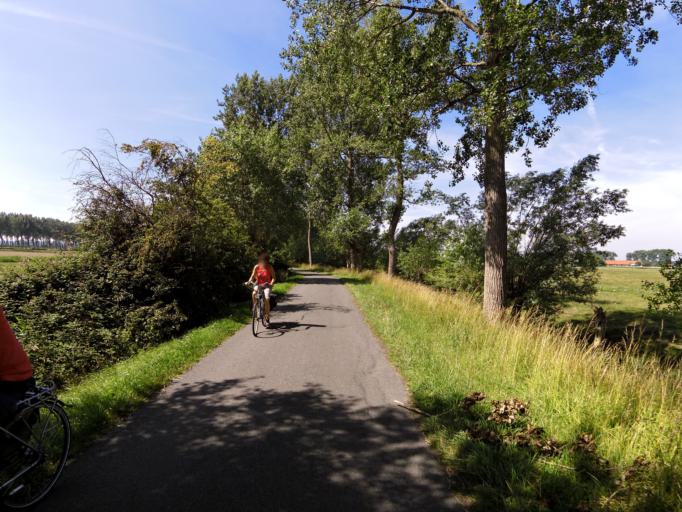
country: BE
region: Flanders
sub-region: Provincie West-Vlaanderen
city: Damme
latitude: 51.2887
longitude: 3.3248
